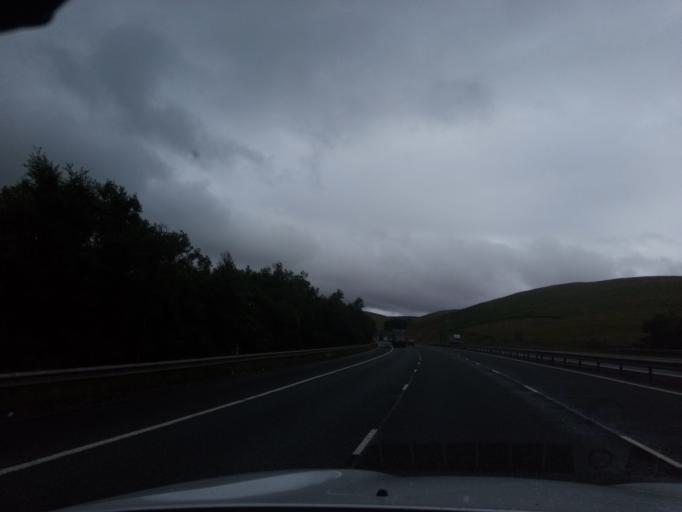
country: GB
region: Scotland
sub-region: South Lanarkshire
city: Douglas
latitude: 55.4823
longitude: -3.6964
